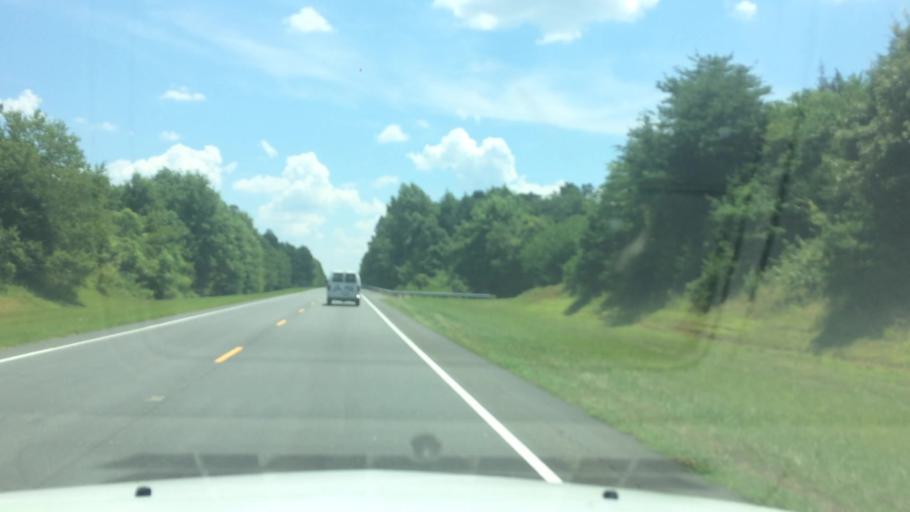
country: US
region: North Carolina
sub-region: Alexander County
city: Stony Point
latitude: 35.8415
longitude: -81.0260
